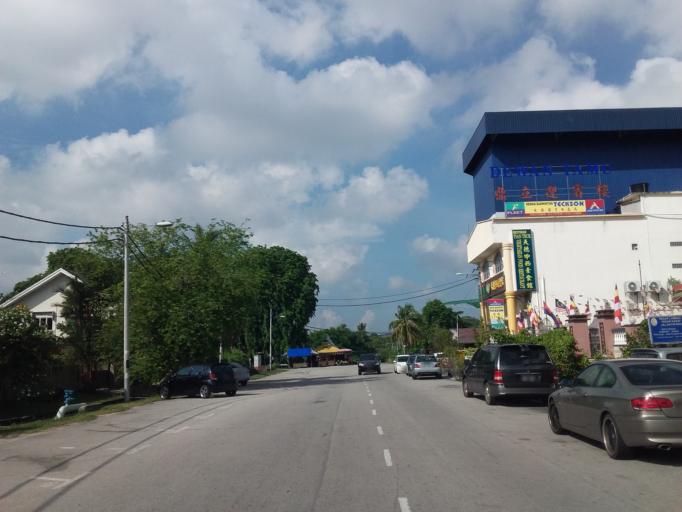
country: MY
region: Johor
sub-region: Daerah Batu Pahat
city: Batu Pahat
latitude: 1.8476
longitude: 102.9272
